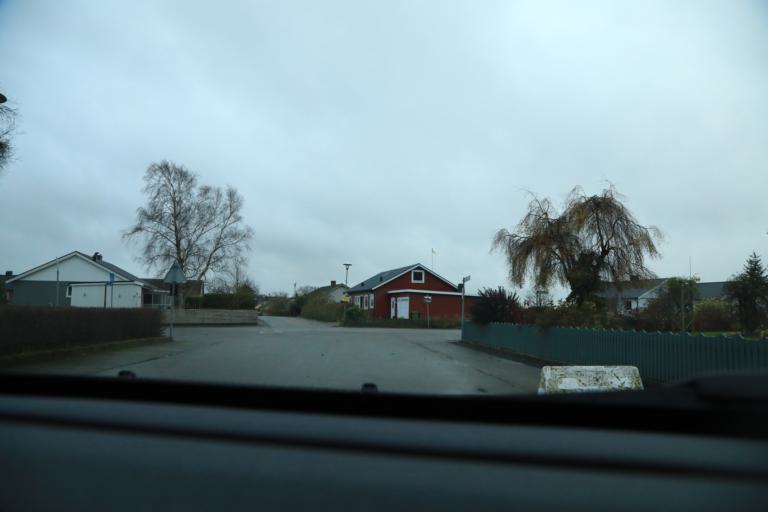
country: SE
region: Halland
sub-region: Varbergs Kommun
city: Varberg
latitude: 57.1731
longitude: 12.2228
